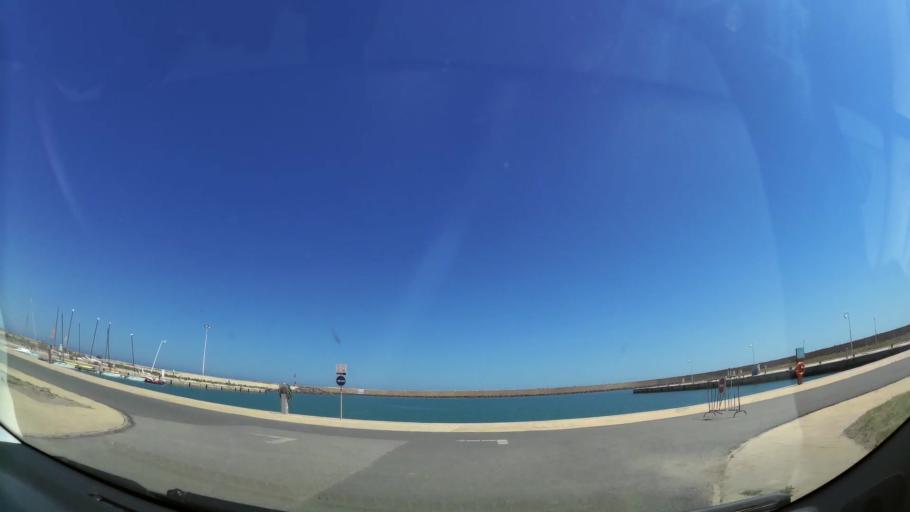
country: MA
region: Oriental
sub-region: Berkane-Taourirt
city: Madagh
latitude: 35.1116
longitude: -2.2950
